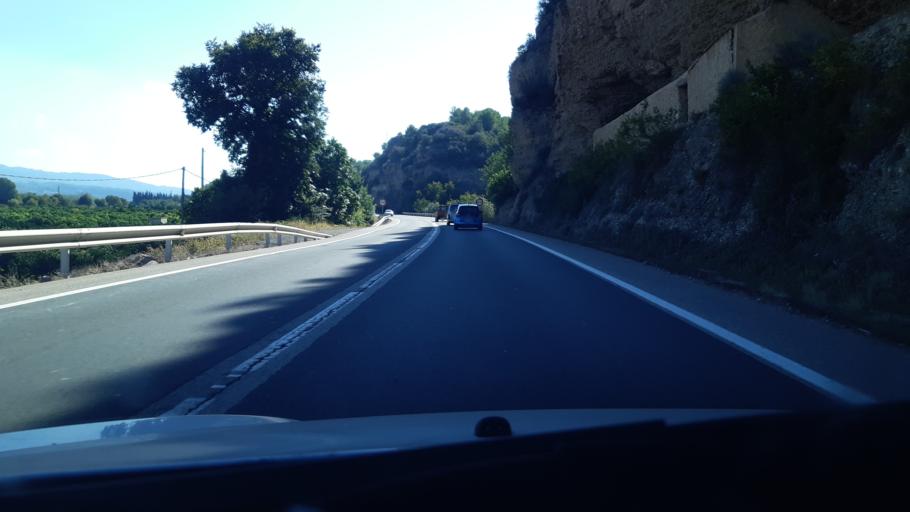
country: ES
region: Catalonia
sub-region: Provincia de Tarragona
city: Tivenys
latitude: 40.8726
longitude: 0.5012
